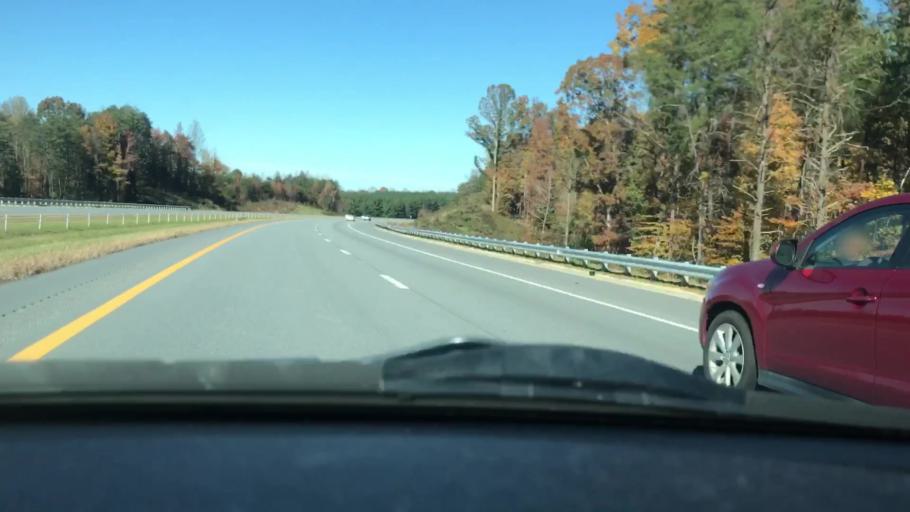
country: US
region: North Carolina
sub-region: Guilford County
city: Oak Ridge
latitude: 36.1572
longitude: -79.9593
